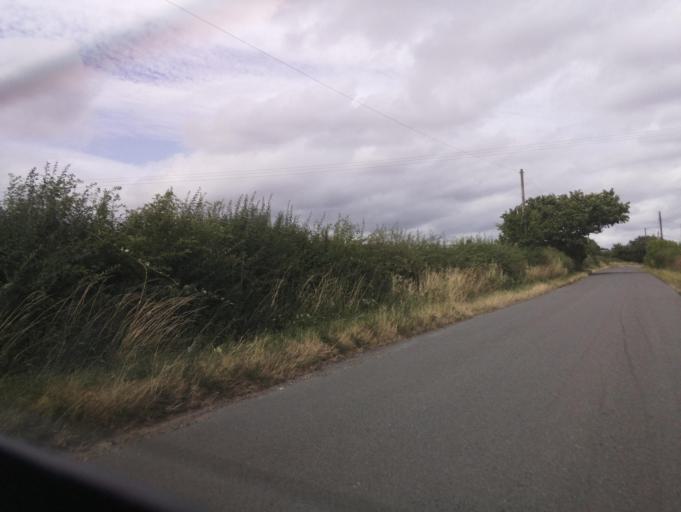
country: GB
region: England
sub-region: Warwickshire
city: Henley in Arden
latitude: 52.2826
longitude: -1.7577
